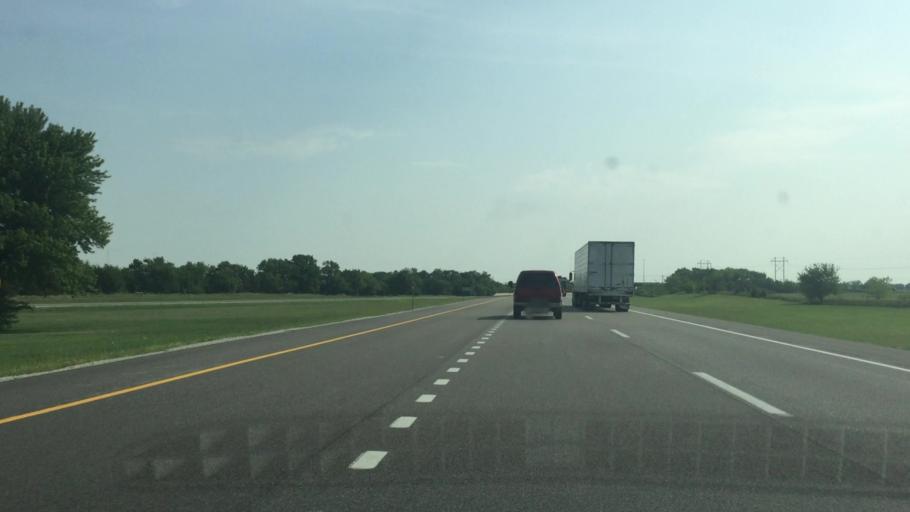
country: US
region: Kansas
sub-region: Butler County
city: Towanda
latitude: 37.7688
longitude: -96.9755
